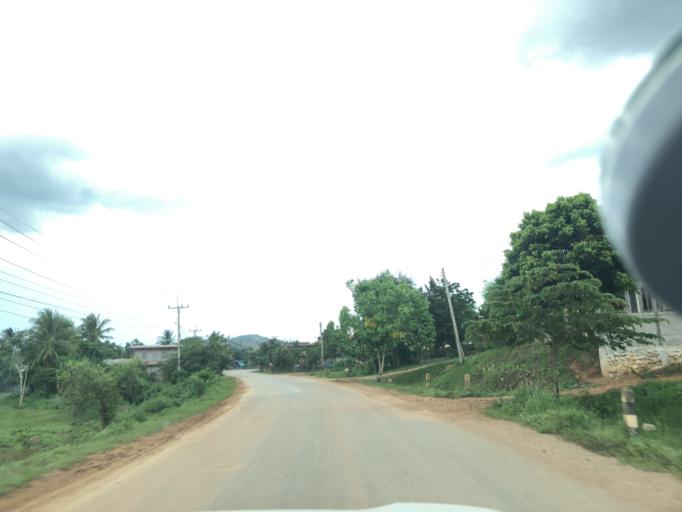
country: TH
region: Uttaradit
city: Ban Khok
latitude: 18.1140
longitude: 101.3723
